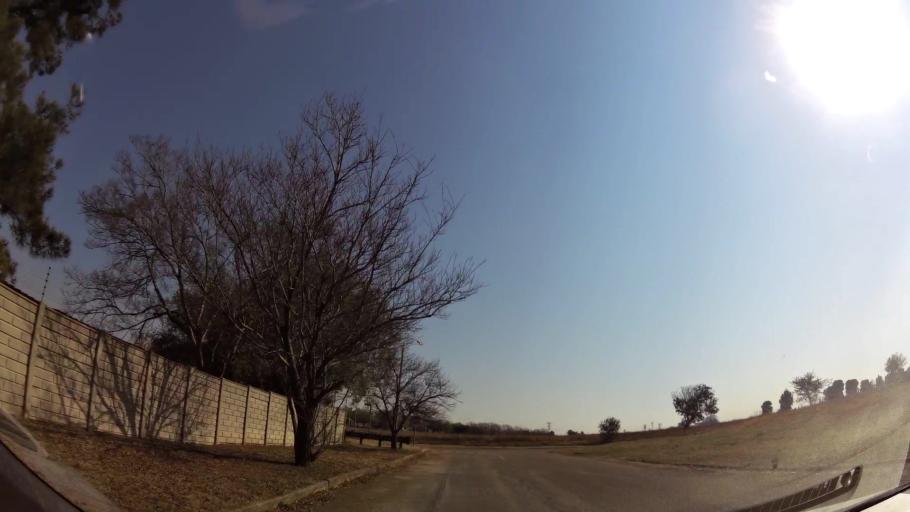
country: ZA
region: Gauteng
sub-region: Ekurhuleni Metropolitan Municipality
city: Boksburg
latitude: -26.2280
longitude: 28.2755
